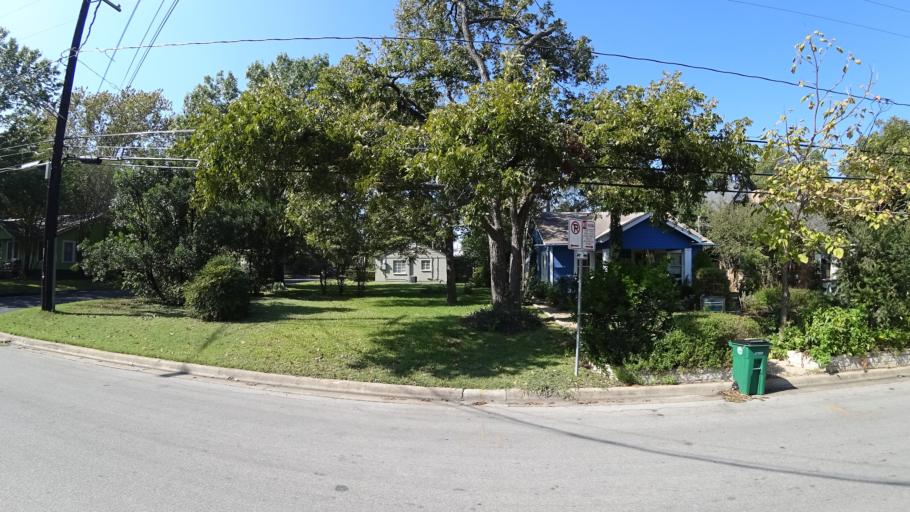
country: US
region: Texas
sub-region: Travis County
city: Austin
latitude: 30.2495
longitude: -97.7700
